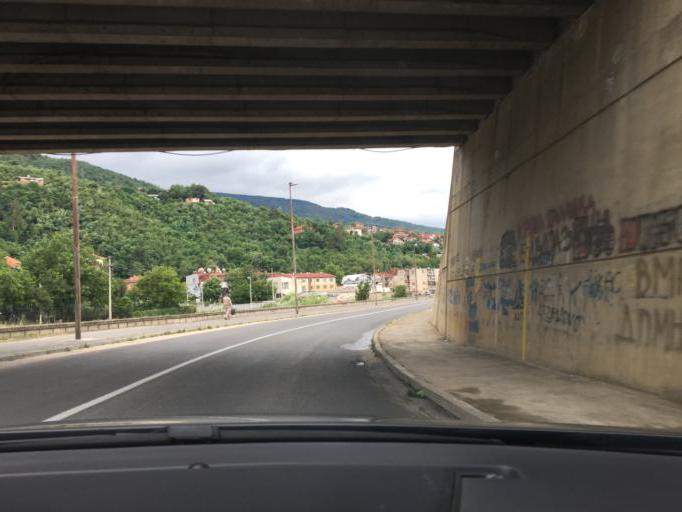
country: MK
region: Kriva Palanka
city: Kriva Palanka
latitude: 42.2022
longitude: 22.3338
